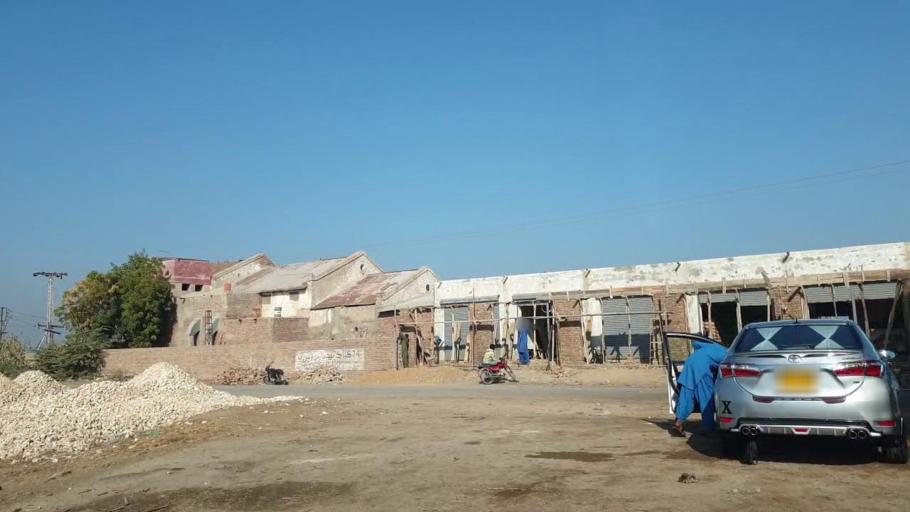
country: PK
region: Sindh
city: Berani
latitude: 25.8111
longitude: 68.9424
